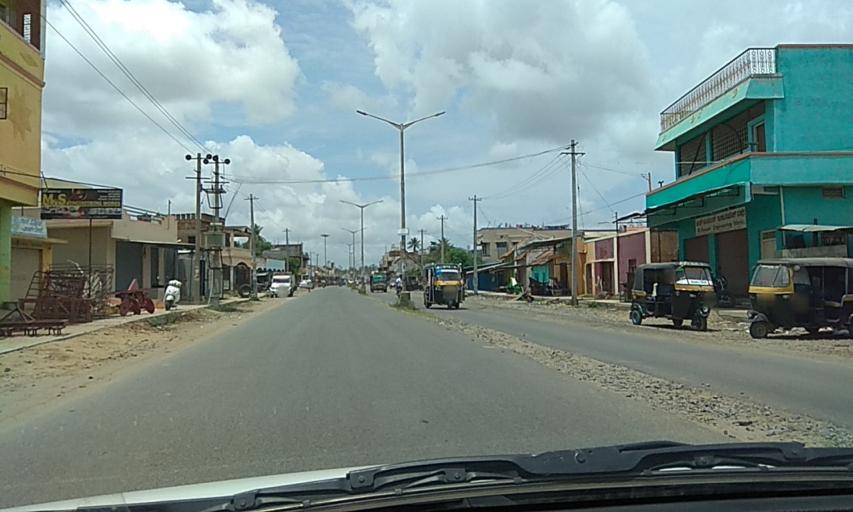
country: IN
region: Karnataka
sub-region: Chamrajnagar
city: Gundlupet
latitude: 11.8090
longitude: 76.6954
